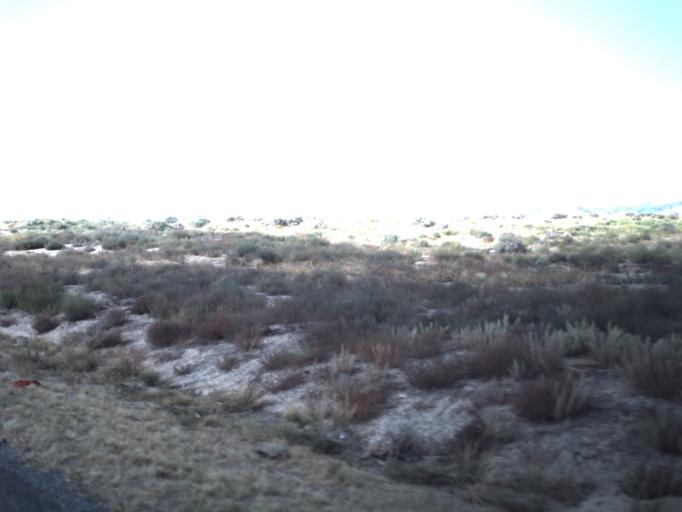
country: US
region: Utah
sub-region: Millard County
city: Delta
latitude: 38.9634
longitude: -112.8021
